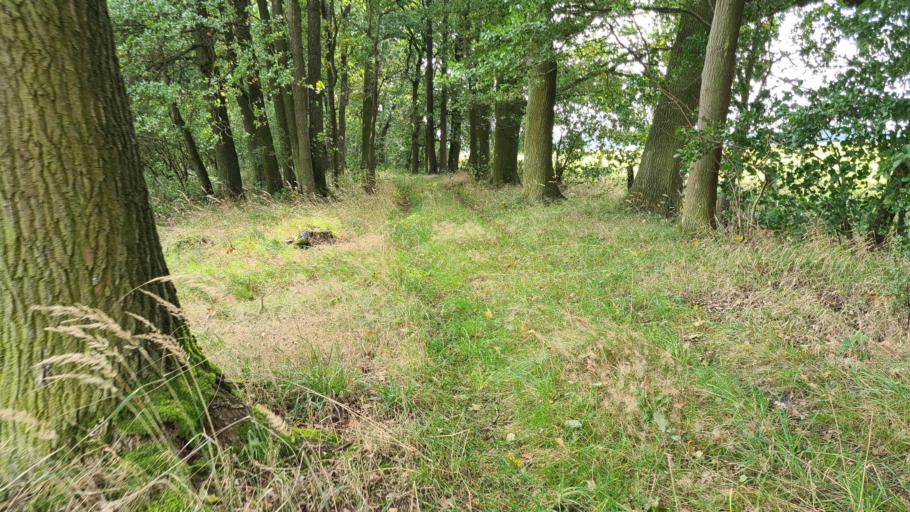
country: DE
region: Brandenburg
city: Schonewalde
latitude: 51.7141
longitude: 13.6069
